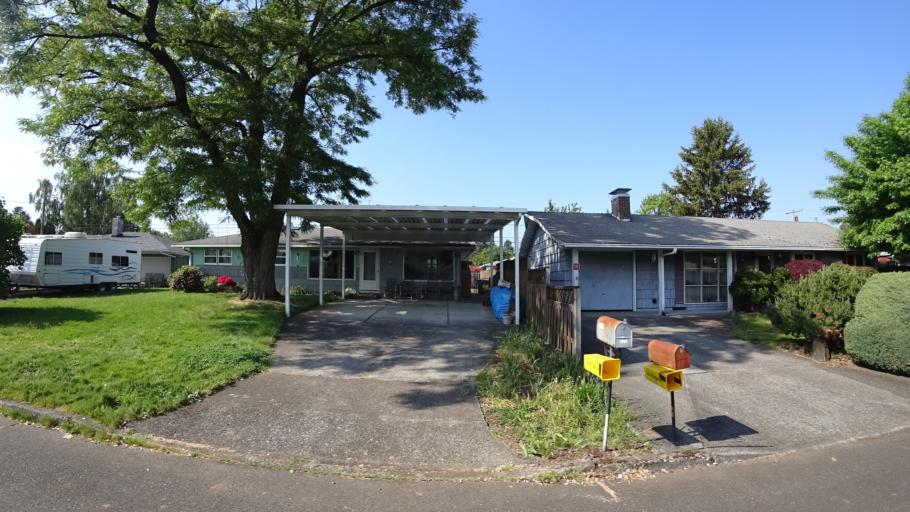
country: US
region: Oregon
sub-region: Multnomah County
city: Gresham
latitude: 45.5123
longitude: -122.5013
